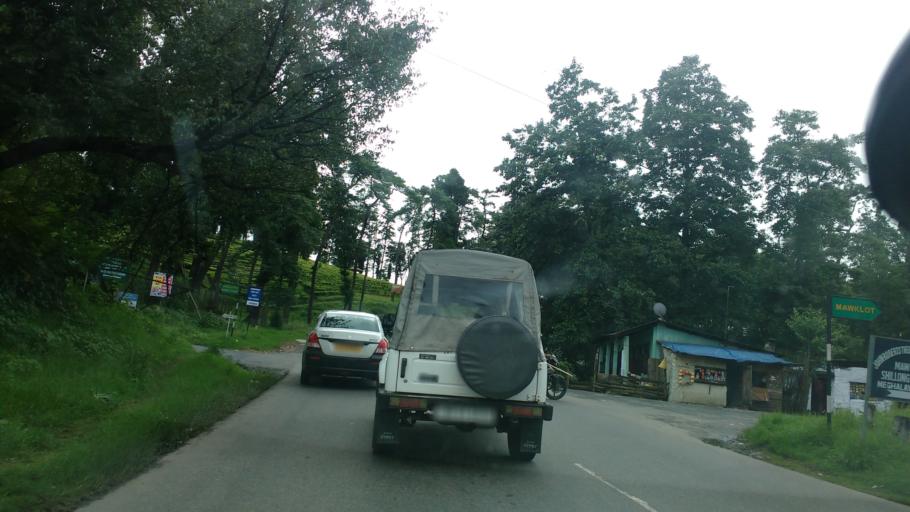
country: IN
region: Meghalaya
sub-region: East Khasi Hills
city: Shillong
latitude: 25.5491
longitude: 91.8416
